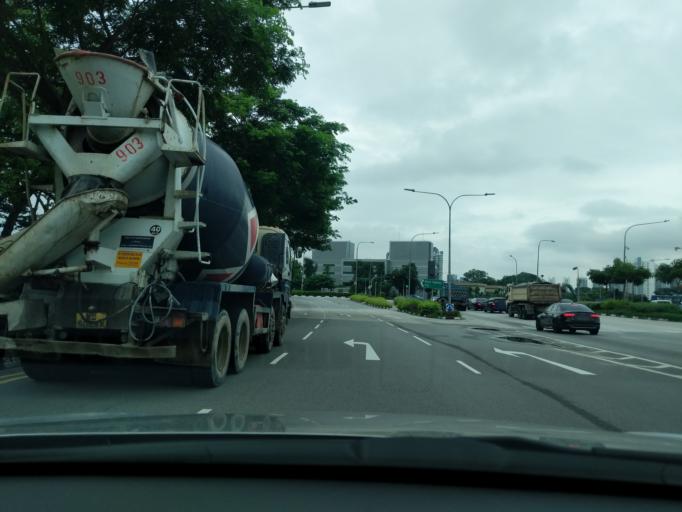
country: SG
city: Singapore
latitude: 1.3076
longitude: 103.8781
